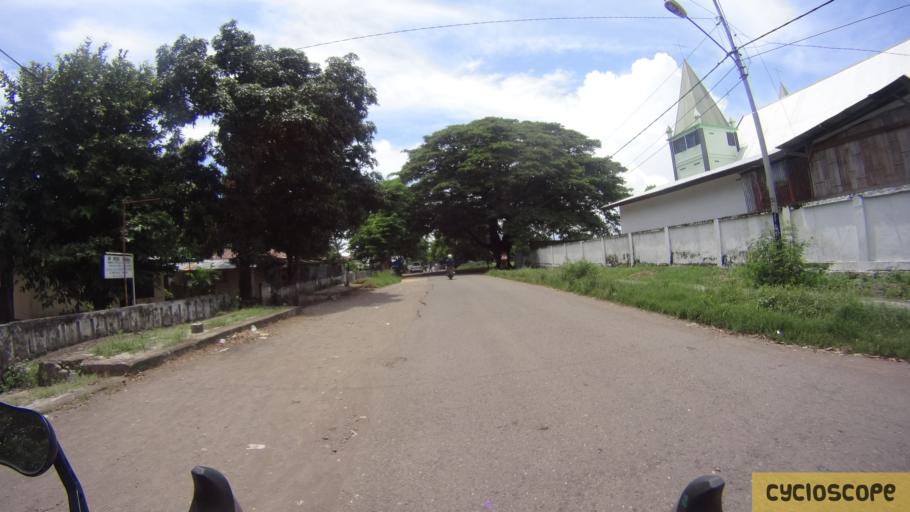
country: ID
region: East Nusa Tenggara
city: Kabor
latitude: -8.6238
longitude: 122.2191
